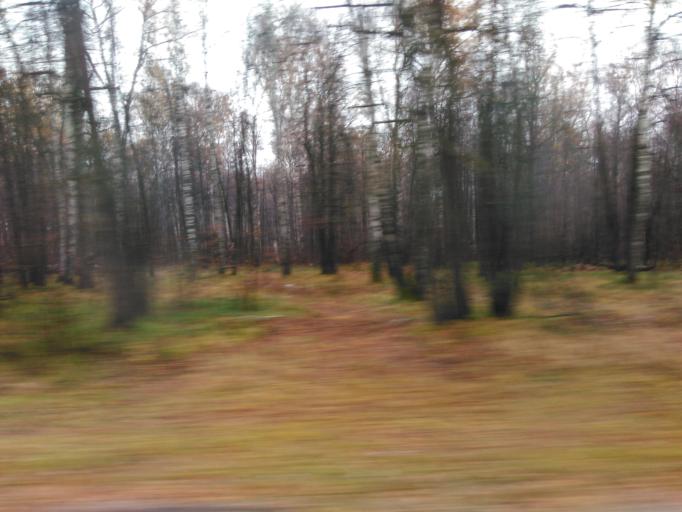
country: RU
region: Tatarstan
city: Osinovo
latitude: 55.8410
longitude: 48.8913
